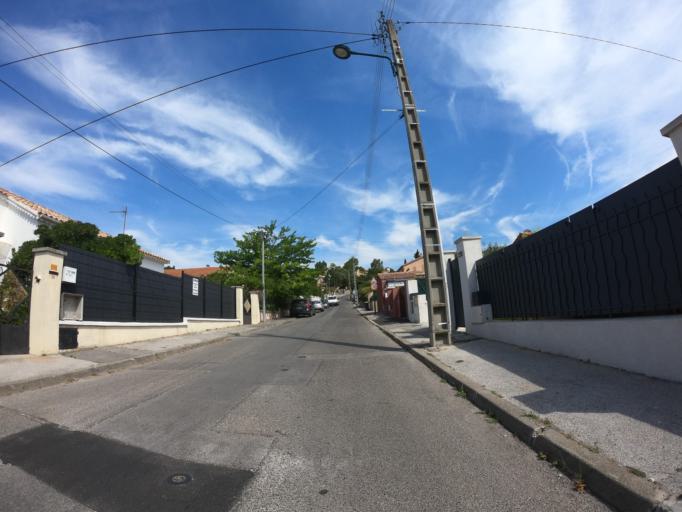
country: FR
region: Provence-Alpes-Cote d'Azur
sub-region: Departement du Var
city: La Garde
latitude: 43.1211
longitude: 5.9985
